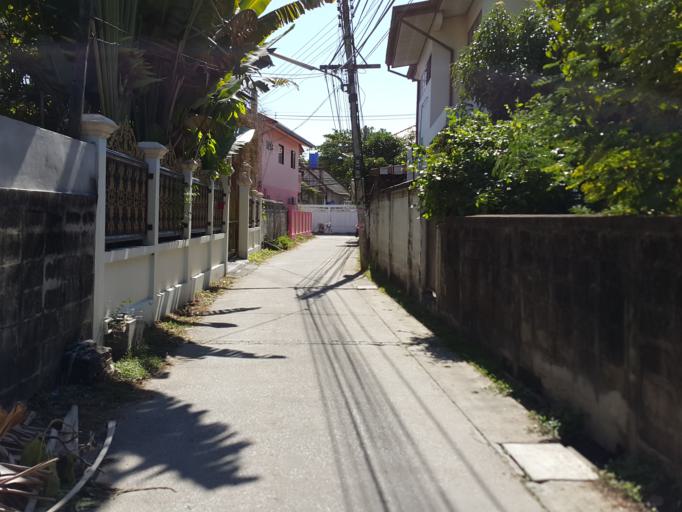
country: TH
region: Chiang Mai
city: Chiang Mai
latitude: 18.7942
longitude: 98.9851
